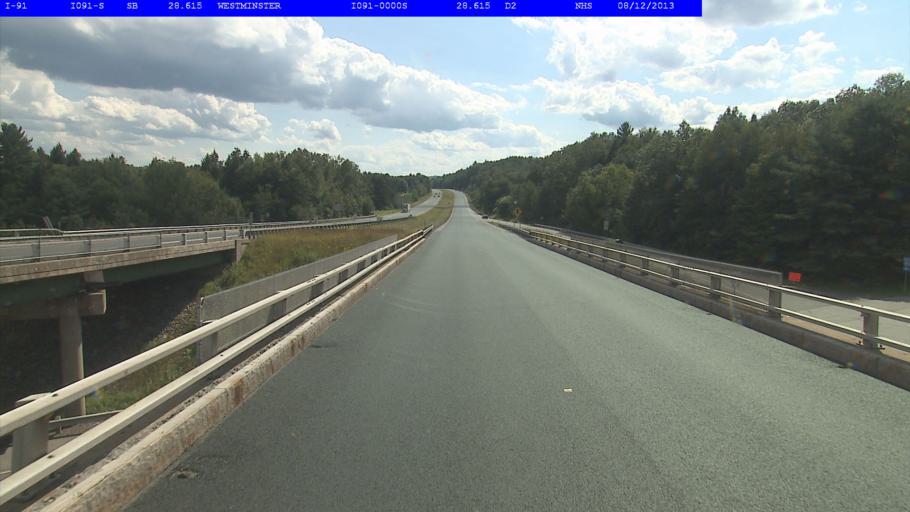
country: US
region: Vermont
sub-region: Windham County
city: Bellows Falls
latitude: 43.0914
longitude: -72.4563
